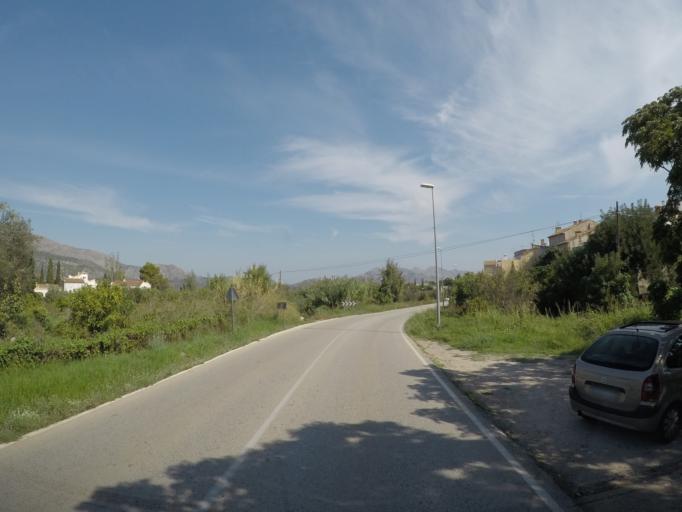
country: ES
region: Valencia
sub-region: Provincia de Alicante
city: Orba
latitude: 38.7807
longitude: -0.0656
